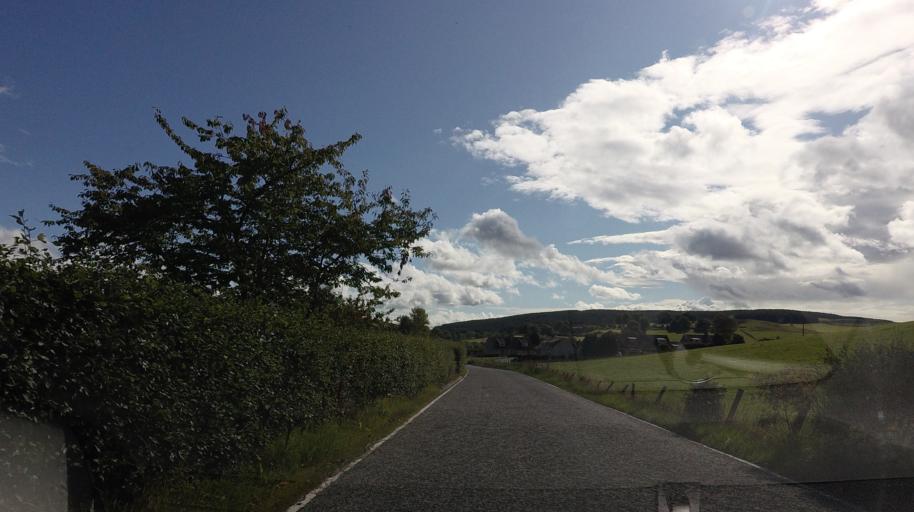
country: GB
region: Scotland
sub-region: Aberdeenshire
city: Torphins
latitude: 57.1316
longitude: -2.6931
